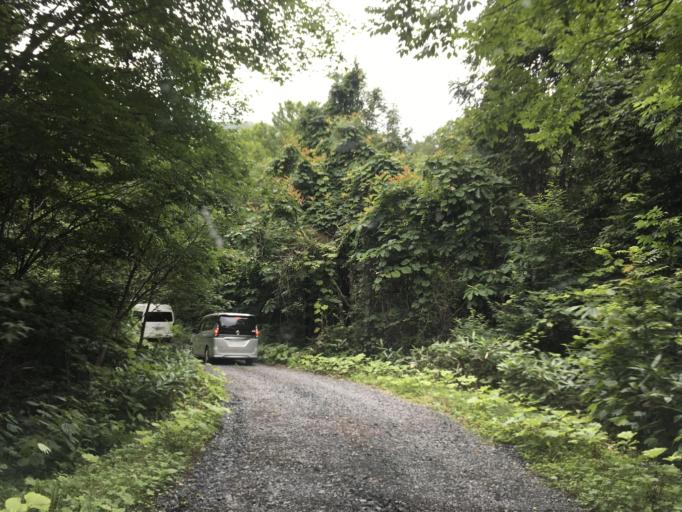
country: JP
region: Iwate
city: Ichinoseki
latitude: 38.9554
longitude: 140.8481
